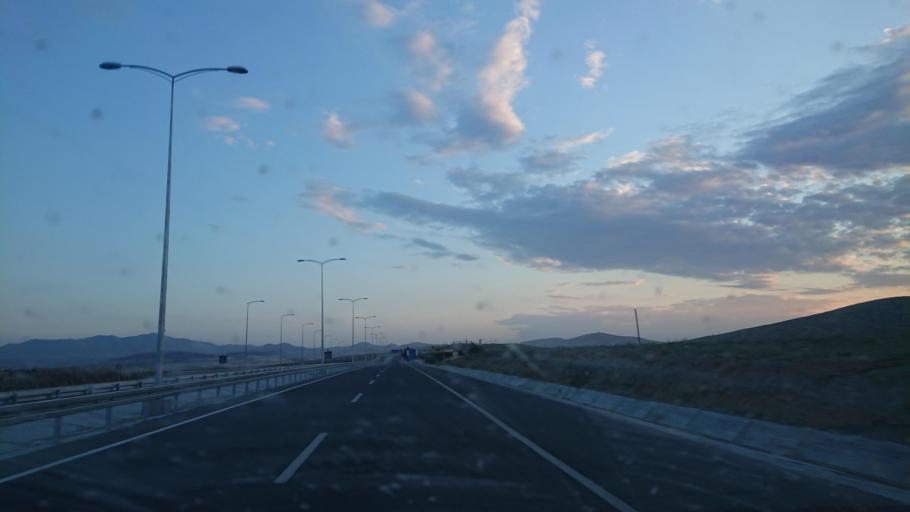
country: TR
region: Aksaray
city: Balci
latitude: 38.7779
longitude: 34.1126
